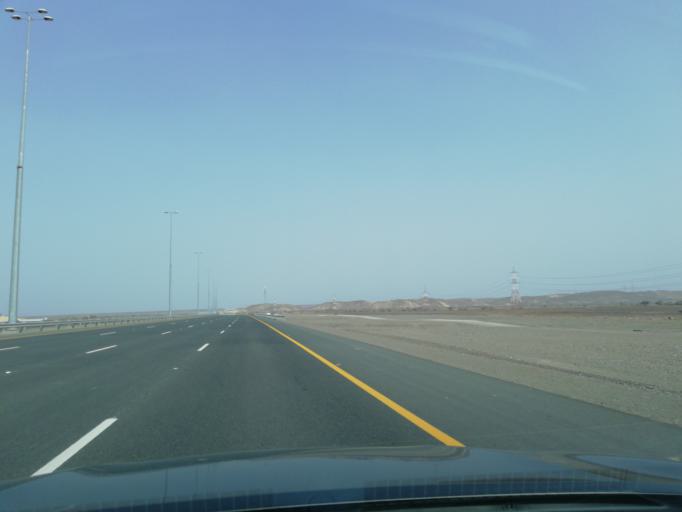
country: OM
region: Al Batinah
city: Al Sohar
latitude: 24.3087
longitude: 56.5897
